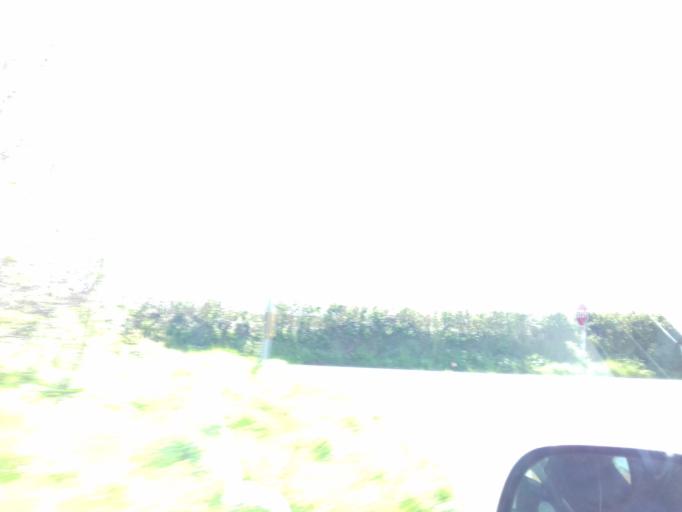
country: IE
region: Munster
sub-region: Waterford
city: Dunmore East
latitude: 52.2354
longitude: -6.8568
